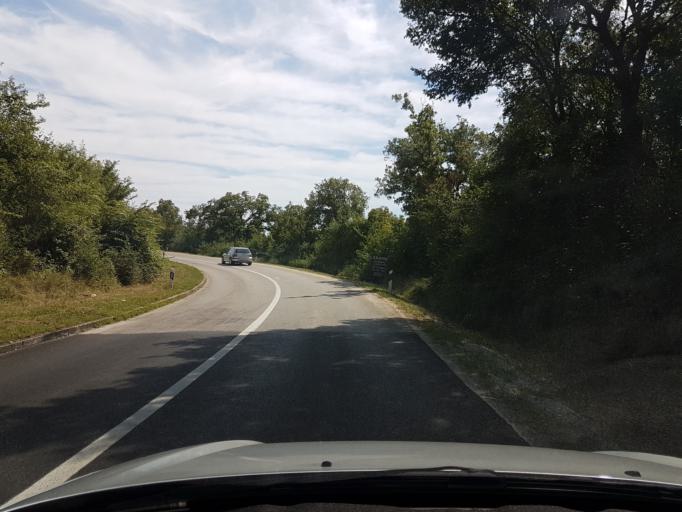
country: HR
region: Istarska
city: Vrsar
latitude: 45.1521
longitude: 13.6943
